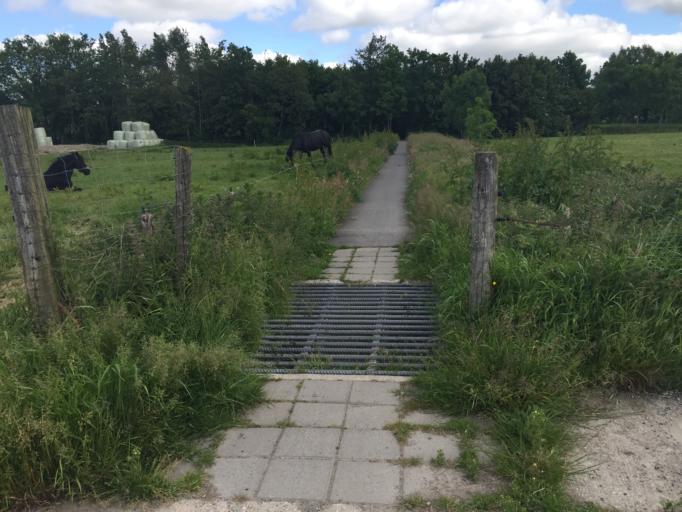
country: NL
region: Friesland
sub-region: Gemeente Leeuwarden
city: Camminghaburen
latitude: 53.2423
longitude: 5.8339
